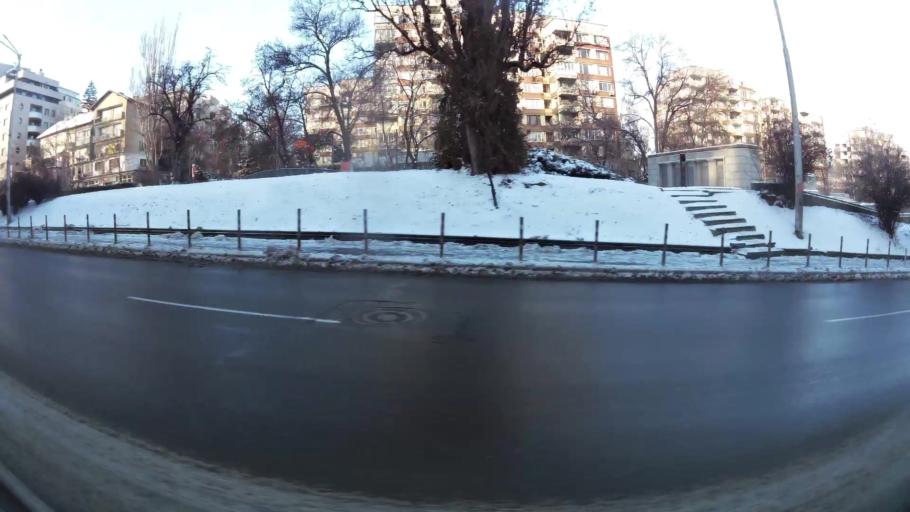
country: BG
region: Sofia-Capital
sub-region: Stolichna Obshtina
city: Sofia
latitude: 42.6745
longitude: 23.3221
